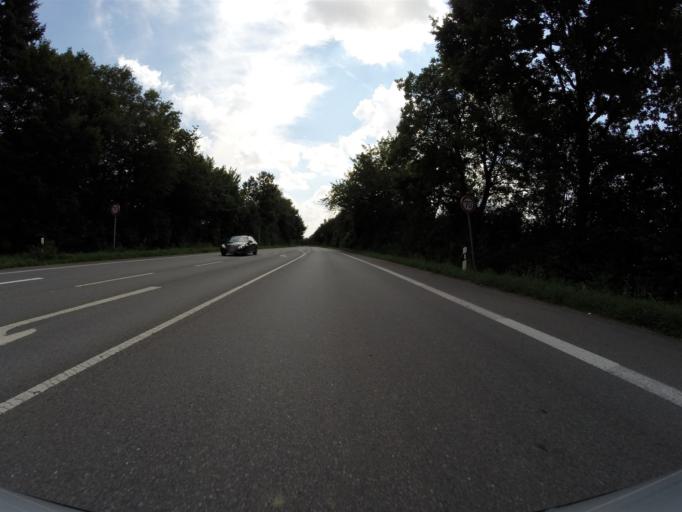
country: DE
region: North Rhine-Westphalia
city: Buende
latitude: 52.1953
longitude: 8.5477
